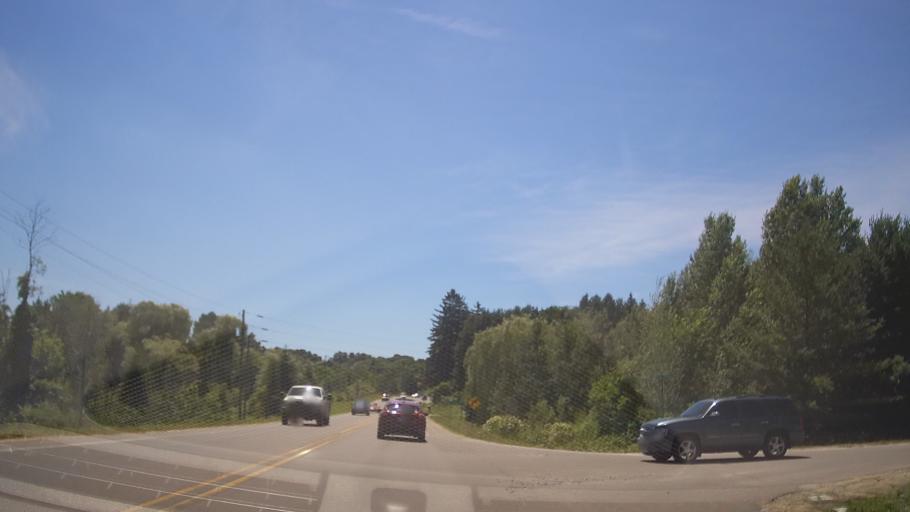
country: US
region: Michigan
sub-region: Grand Traverse County
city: Traverse City
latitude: 44.7307
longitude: -85.6619
